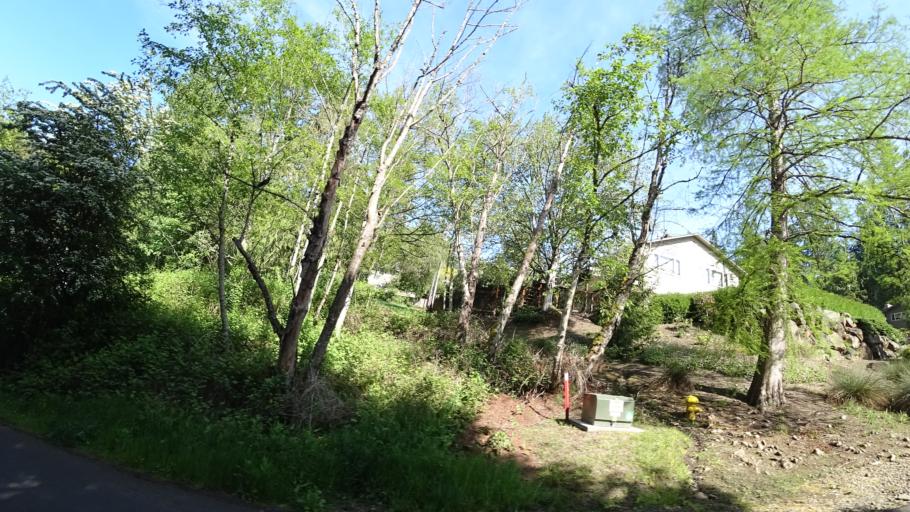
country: US
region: Oregon
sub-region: Washington County
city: West Slope
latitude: 45.4953
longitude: -122.7453
